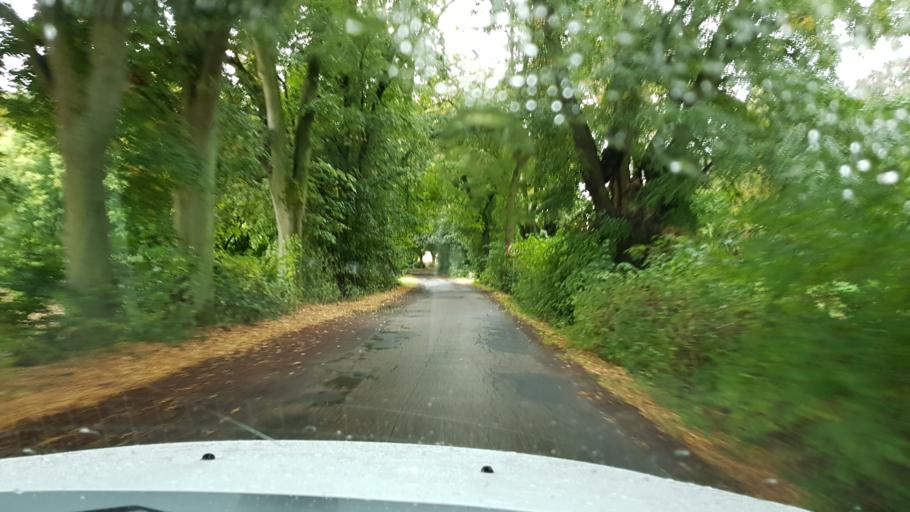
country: DE
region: Brandenburg
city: Meyenburg
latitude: 52.9940
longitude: 14.2758
